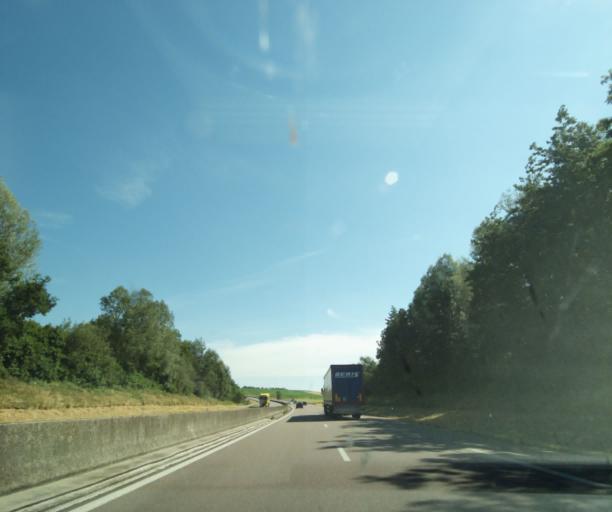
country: FR
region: Lorraine
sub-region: Departement des Vosges
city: Chatenois
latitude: 48.3722
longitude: 5.8761
